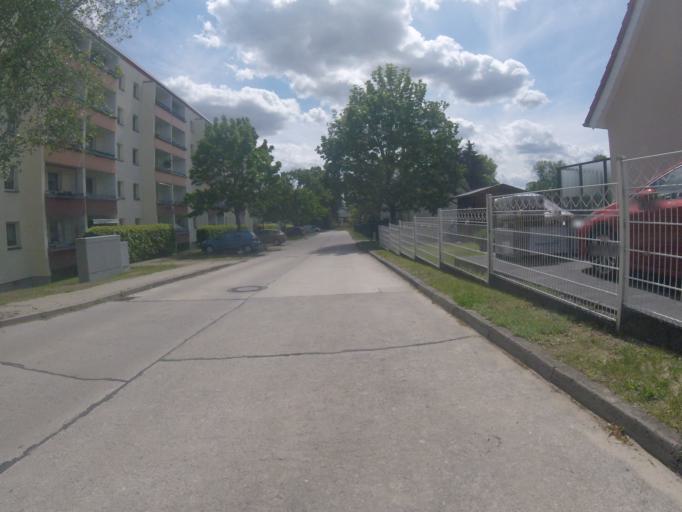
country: DE
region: Brandenburg
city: Konigs Wusterhausen
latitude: 52.2986
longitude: 13.6150
